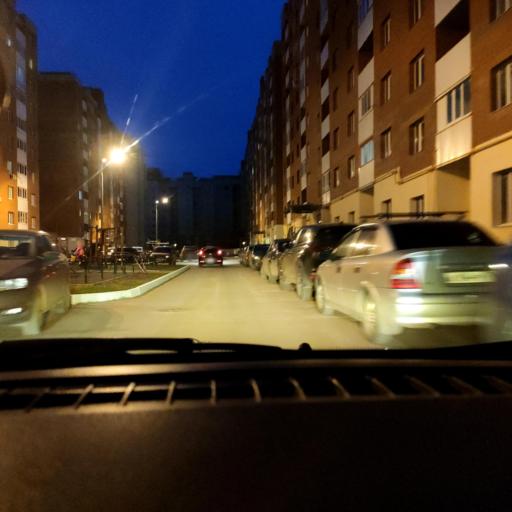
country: RU
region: Samara
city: Petra-Dubrava
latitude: 53.3076
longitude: 50.2857
